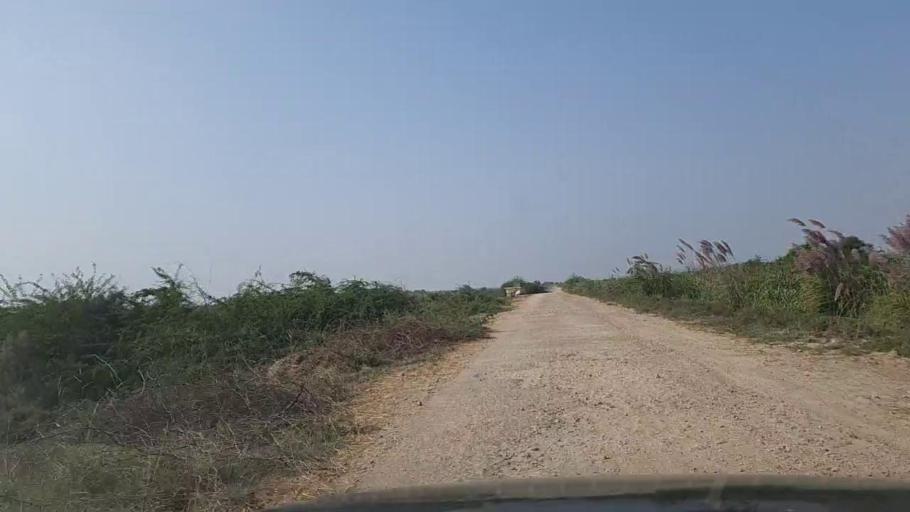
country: PK
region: Sindh
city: Gharo
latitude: 24.7346
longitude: 67.7398
